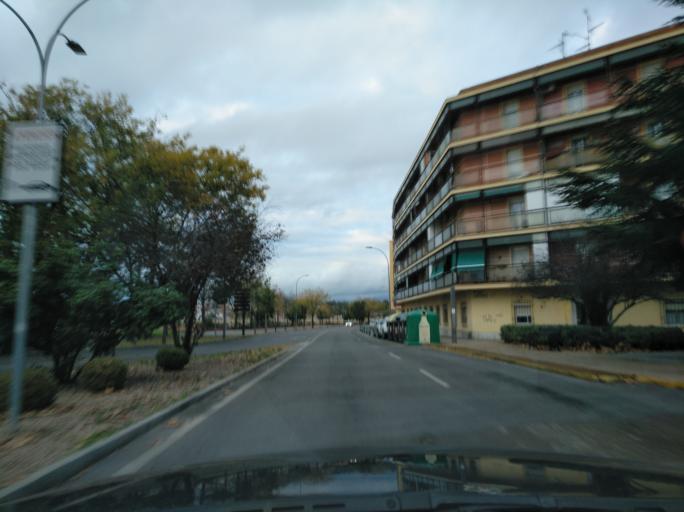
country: ES
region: Extremadura
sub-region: Provincia de Badajoz
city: Badajoz
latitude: 38.8782
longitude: -6.9802
